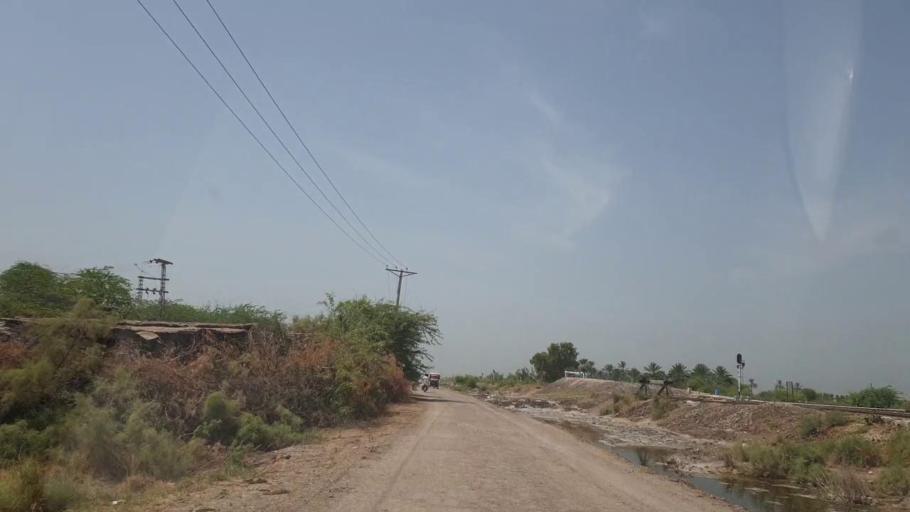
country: PK
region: Sindh
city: Gambat
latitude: 27.3355
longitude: 68.5433
